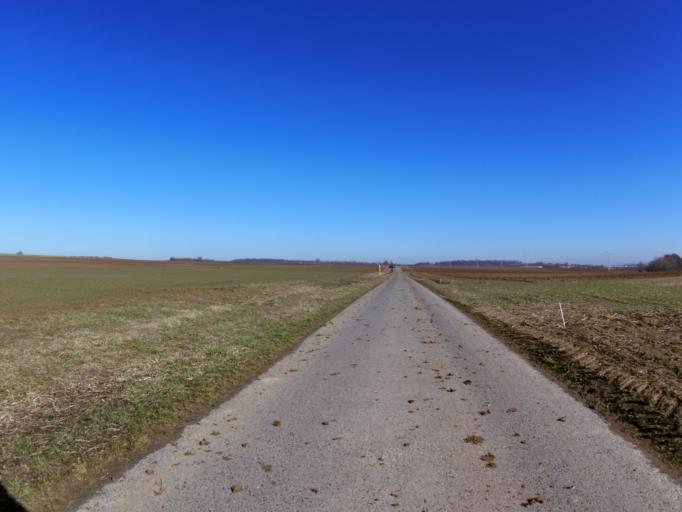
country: DE
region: Bavaria
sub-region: Regierungsbezirk Unterfranken
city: Estenfeld
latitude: 49.8377
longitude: 9.9908
